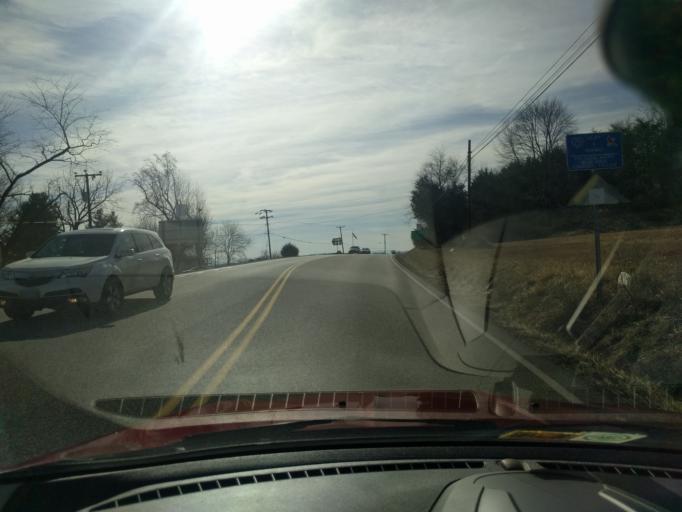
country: US
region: Virginia
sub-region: Augusta County
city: Weyers Cave
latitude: 38.2882
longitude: -78.9358
